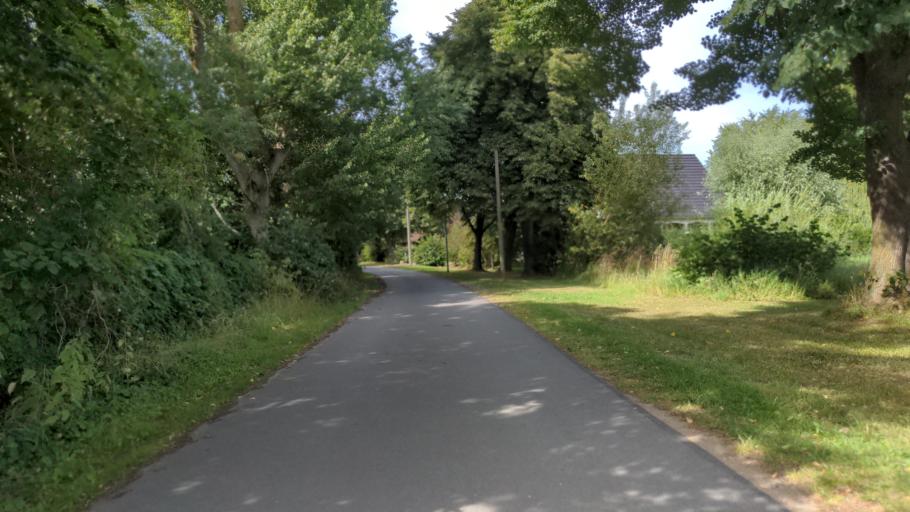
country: DE
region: Mecklenburg-Vorpommern
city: Kalkhorst
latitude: 54.0013
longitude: 11.0817
